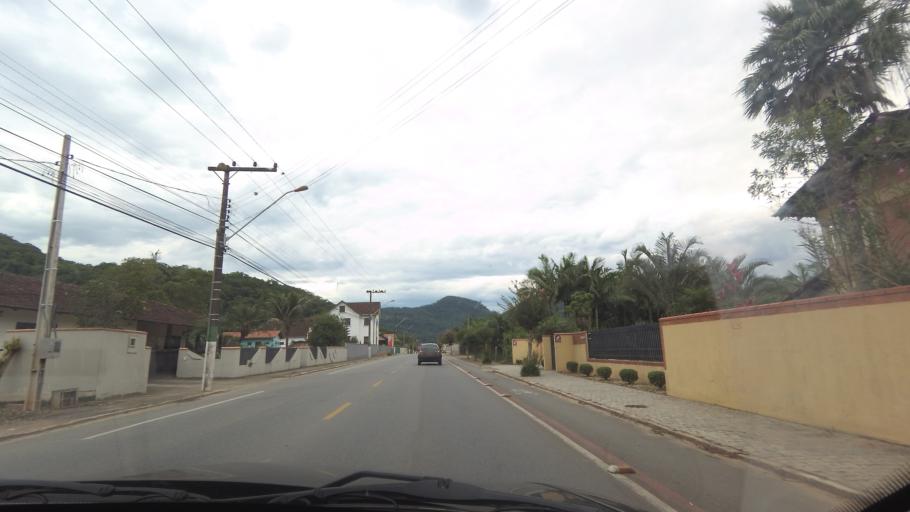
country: BR
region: Santa Catarina
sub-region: Schroeder
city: Schroeder
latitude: -26.4285
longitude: -49.0653
